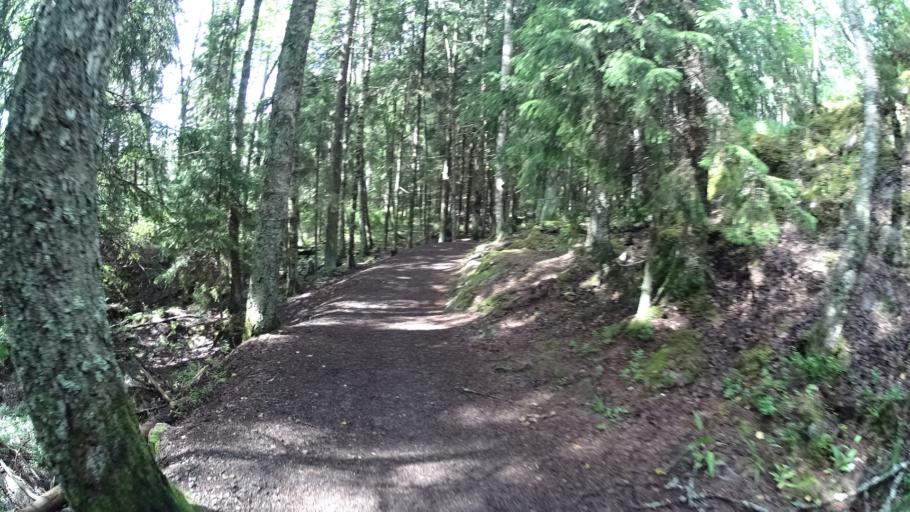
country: FI
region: Uusimaa
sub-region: Helsinki
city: Kauniainen
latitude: 60.3370
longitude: 24.6861
